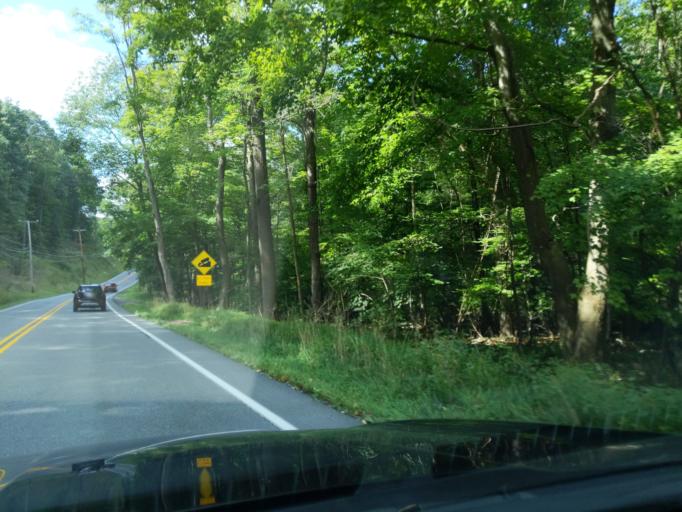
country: US
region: Pennsylvania
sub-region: Blair County
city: Greenwood
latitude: 40.5110
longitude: -78.3593
